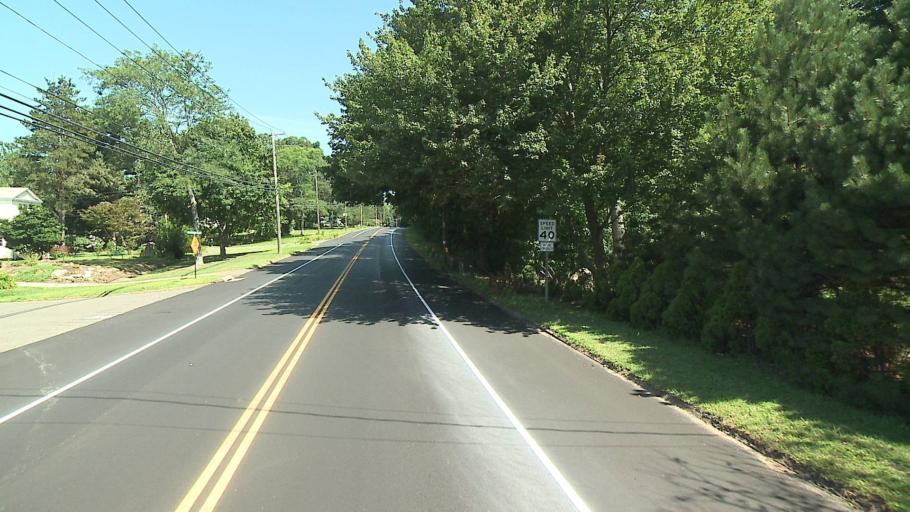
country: US
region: Connecticut
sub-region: Fairfield County
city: Trumbull
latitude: 41.2284
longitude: -73.1777
